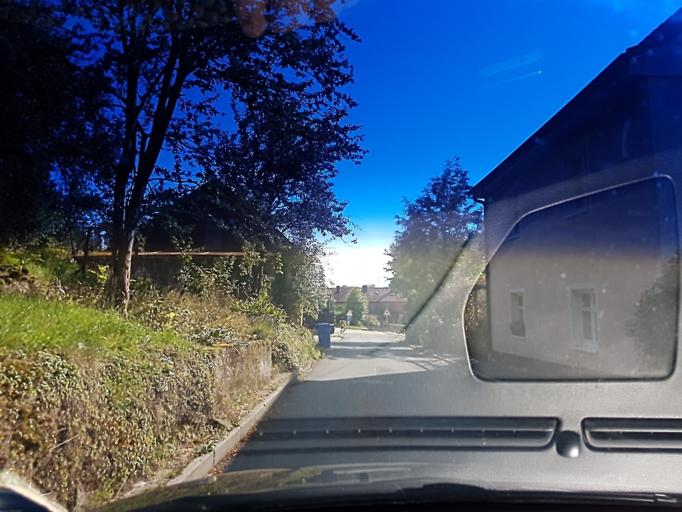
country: DE
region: Bavaria
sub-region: Upper Franconia
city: Kirchenpingarten
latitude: 49.9476
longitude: 11.7576
